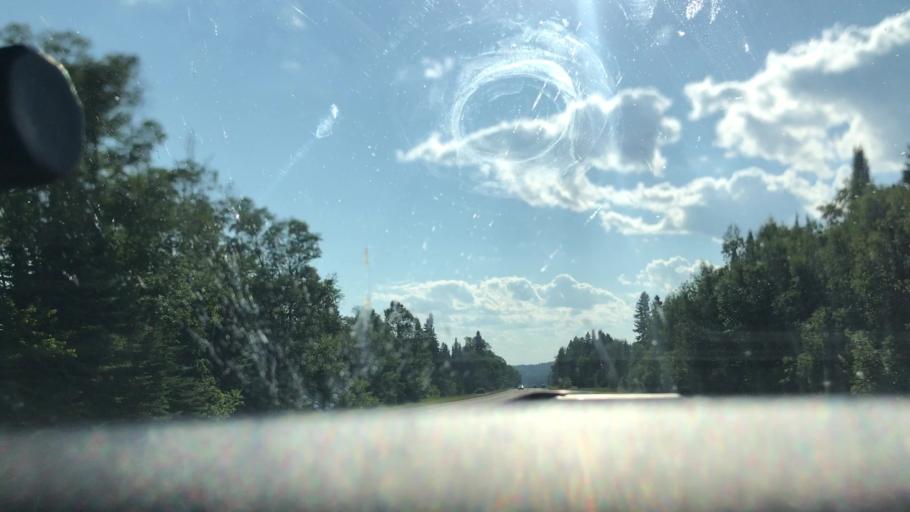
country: US
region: Minnesota
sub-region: Cook County
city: Grand Marais
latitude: 47.7959
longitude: -90.1338
